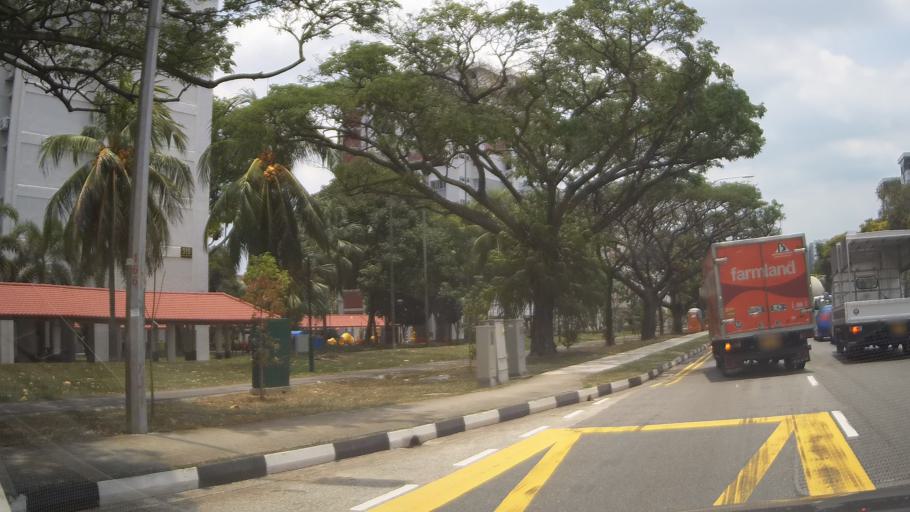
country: SG
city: Singapore
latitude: 1.3077
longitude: 103.7585
